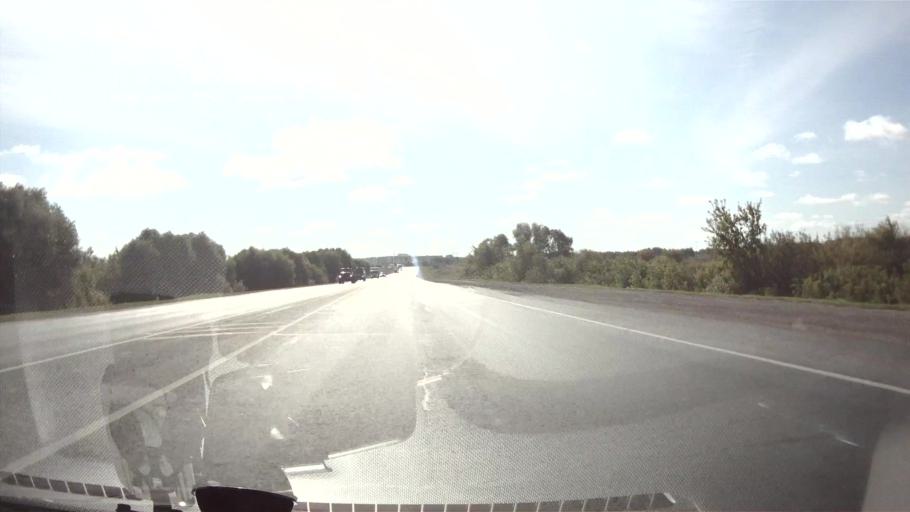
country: RU
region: Ulyanovsk
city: Isheyevka
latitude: 54.3034
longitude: 48.2419
